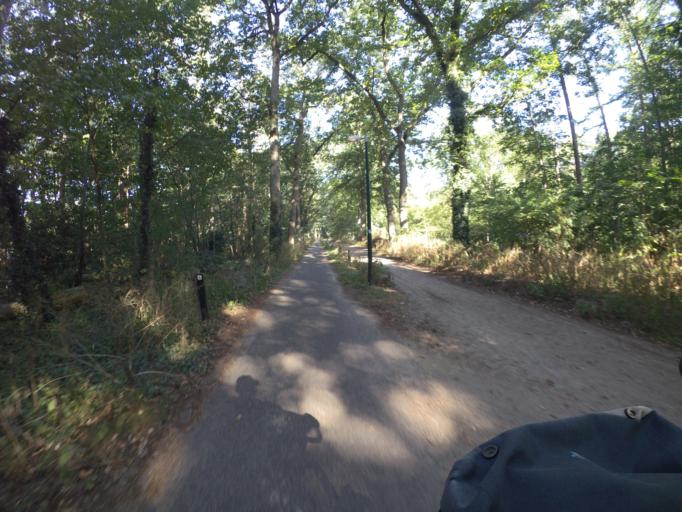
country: NL
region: Gelderland
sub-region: Gemeente Lochem
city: Lochem
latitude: 52.1468
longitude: 6.4150
